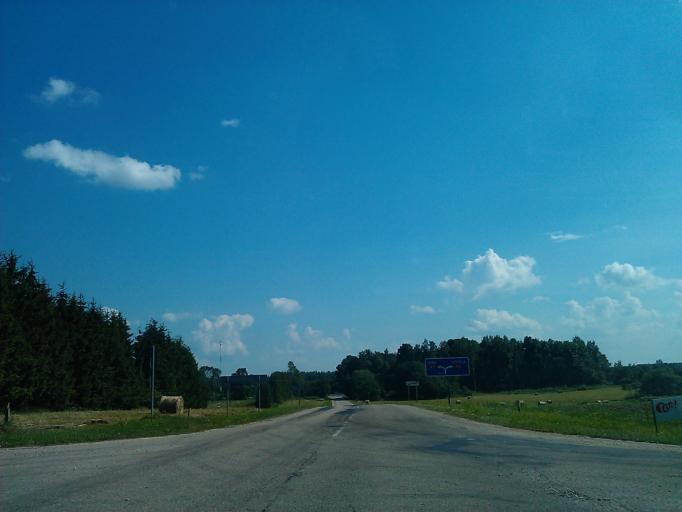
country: LV
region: Aizpute
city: Aizpute
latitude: 56.6050
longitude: 21.7393
